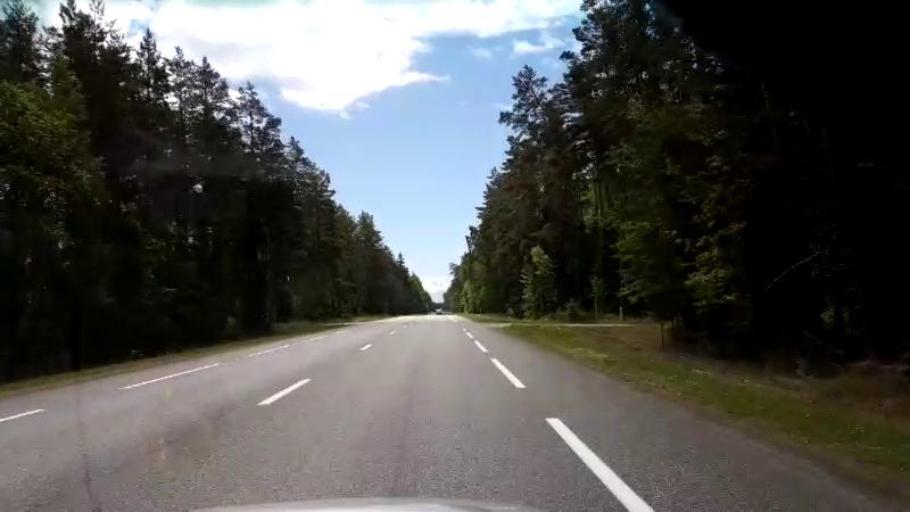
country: LV
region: Saulkrastu
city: Saulkrasti
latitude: 57.4795
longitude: 24.4335
